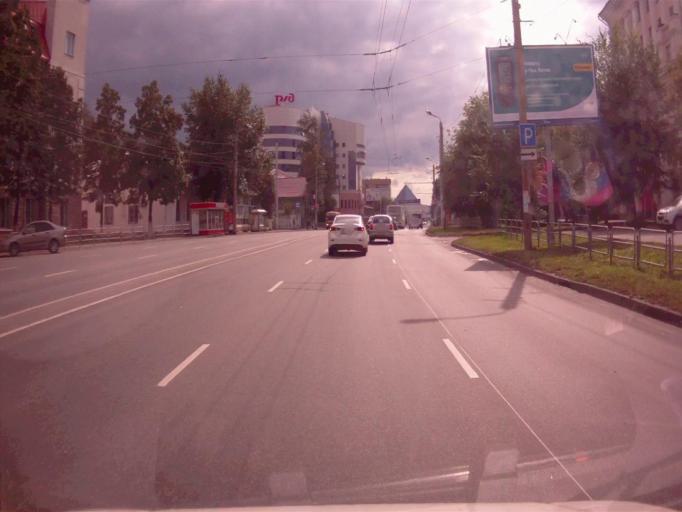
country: RU
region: Chelyabinsk
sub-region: Gorod Chelyabinsk
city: Chelyabinsk
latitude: 55.1463
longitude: 61.4165
